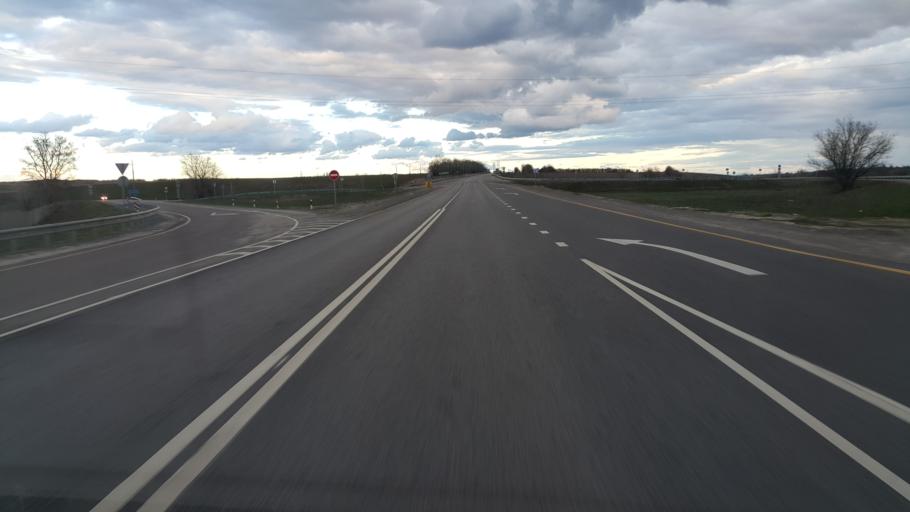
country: RU
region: Volgograd
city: Mikhaylovka
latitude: 49.9929
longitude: 43.2518
